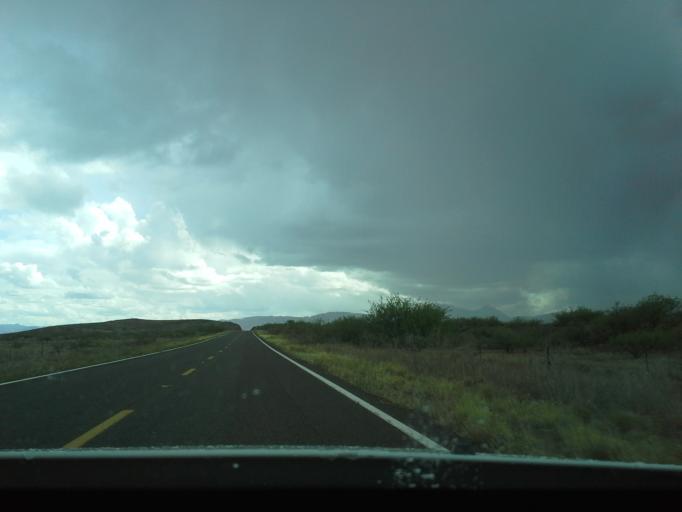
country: US
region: Arizona
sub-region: Cochise County
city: Douglas
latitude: 31.5434
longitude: -109.2846
